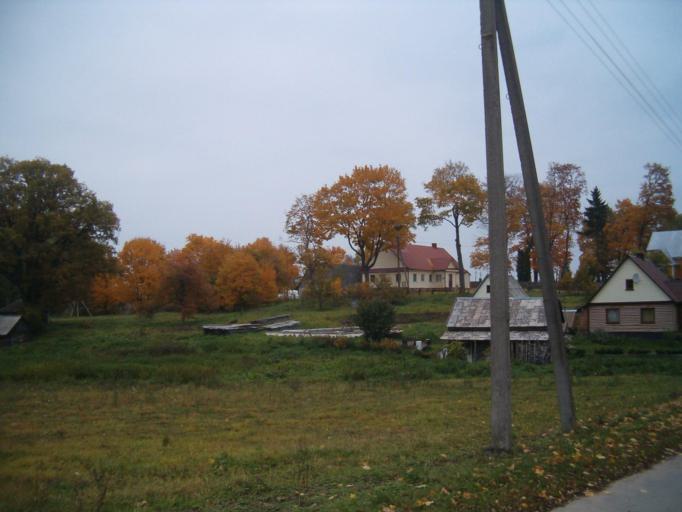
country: LT
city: Zarasai
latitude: 55.7541
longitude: 26.0261
